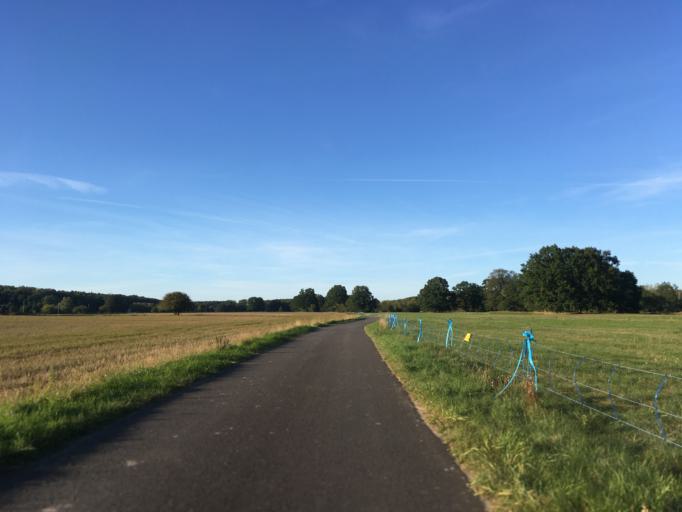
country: PL
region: Lubusz
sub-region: Powiat zarski
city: Trzebiel
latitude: 51.6311
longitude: 14.7539
